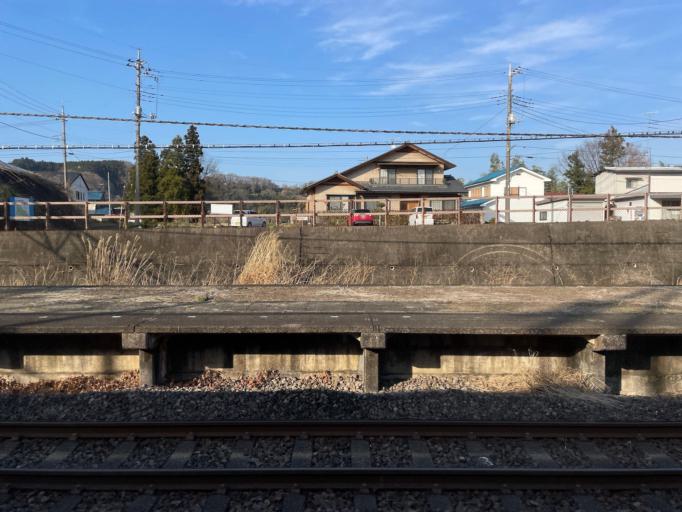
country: JP
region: Gunma
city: Annaka
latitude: 36.3097
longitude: 138.7970
